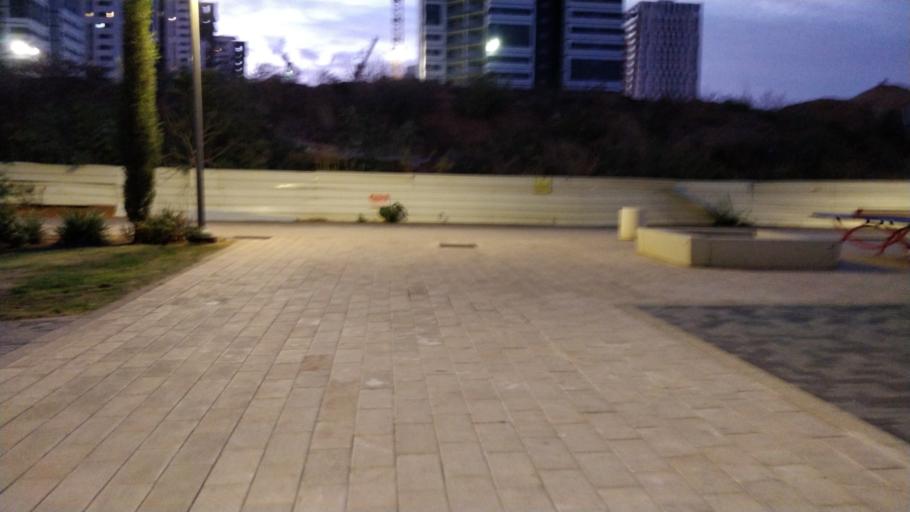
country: IL
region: Central District
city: Ganne Tiqwa
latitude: 32.0656
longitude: 34.8772
